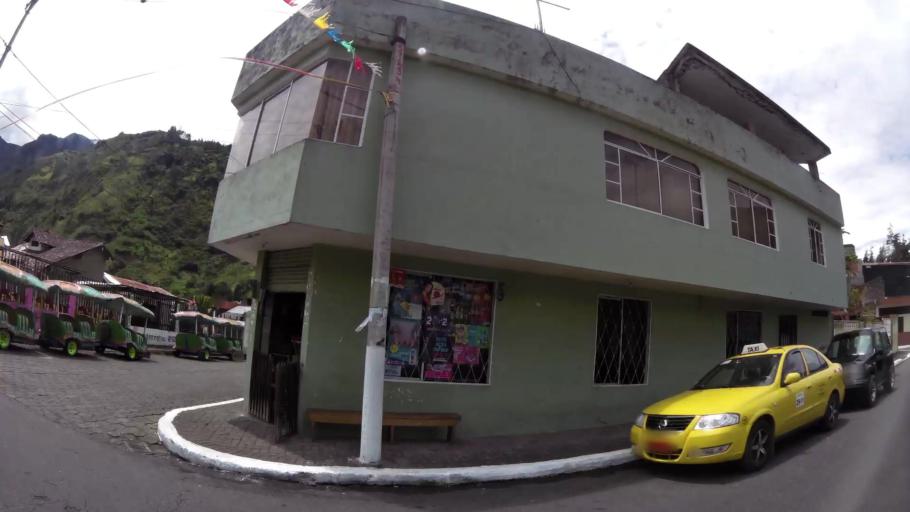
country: EC
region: Tungurahua
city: Banos
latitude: -1.3919
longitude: -78.4137
